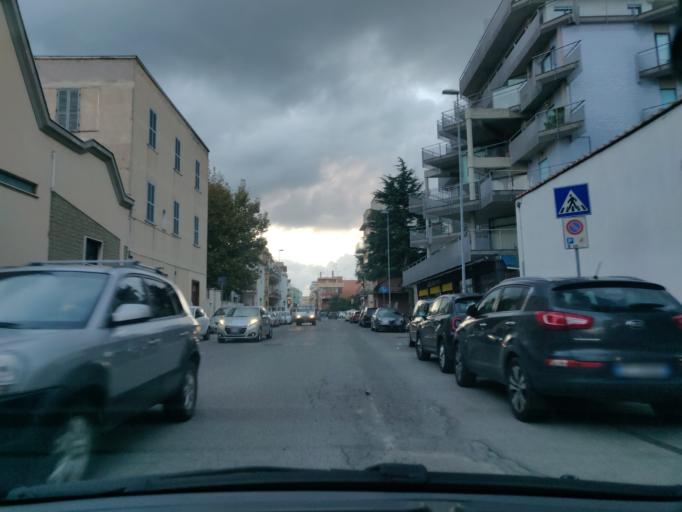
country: IT
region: Latium
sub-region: Citta metropolitana di Roma Capitale
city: Civitavecchia
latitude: 42.0958
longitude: 11.8031
